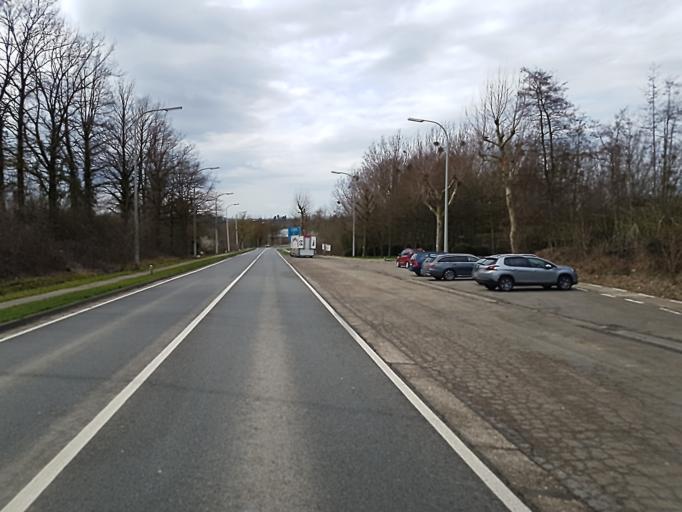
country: BE
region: Flanders
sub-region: Provincie Limburg
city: Borgloon
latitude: 50.7988
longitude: 5.3465
